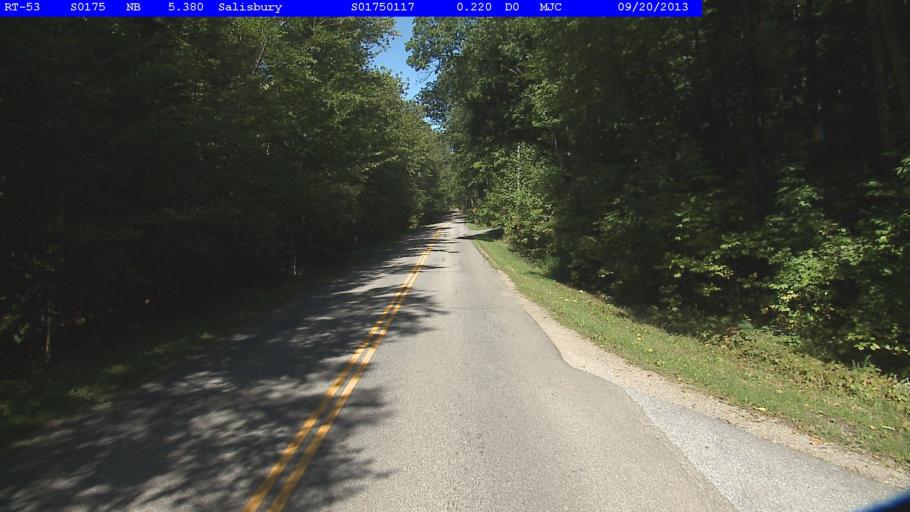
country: US
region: Vermont
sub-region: Rutland County
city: Brandon
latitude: 43.9008
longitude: -73.0644
